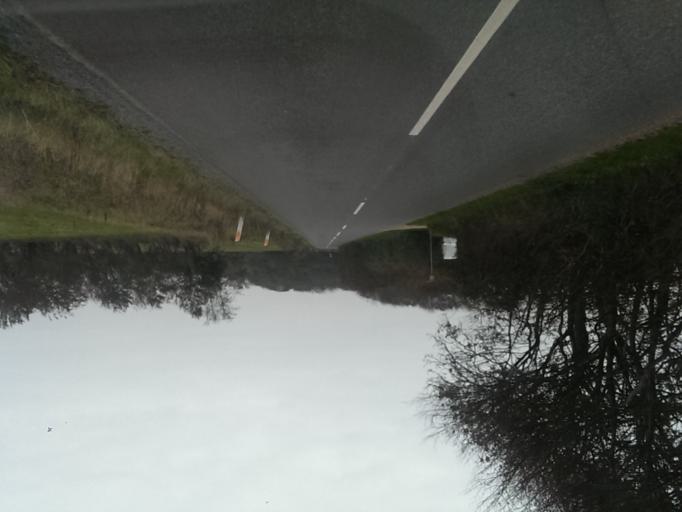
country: DK
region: South Denmark
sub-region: Esbjerg Kommune
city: Tjaereborg
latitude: 55.4980
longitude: 8.5226
